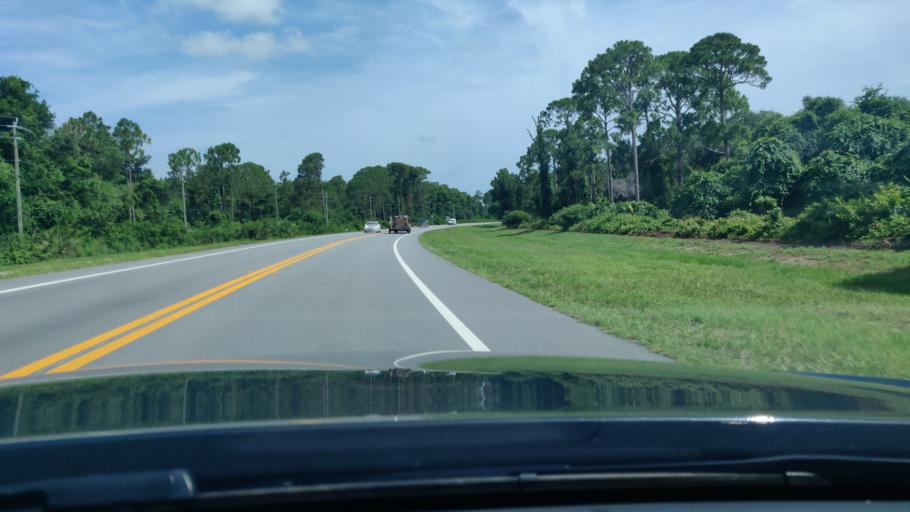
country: US
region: Florida
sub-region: Flagler County
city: Palm Coast
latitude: 29.5363
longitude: -81.1732
